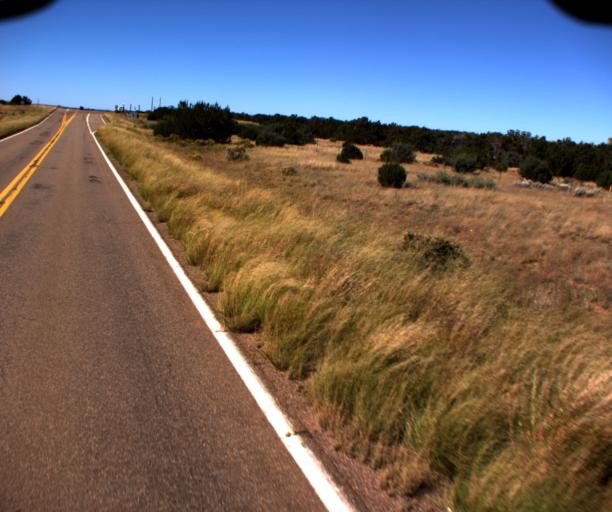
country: US
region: Arizona
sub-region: Navajo County
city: Heber-Overgaard
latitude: 34.4816
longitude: -110.3361
